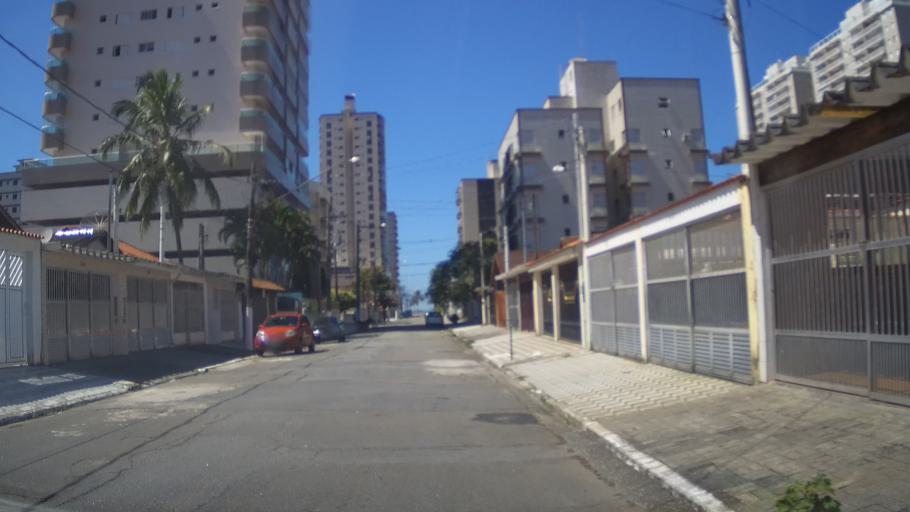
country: BR
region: Sao Paulo
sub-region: Praia Grande
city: Praia Grande
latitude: -24.0251
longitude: -46.4703
